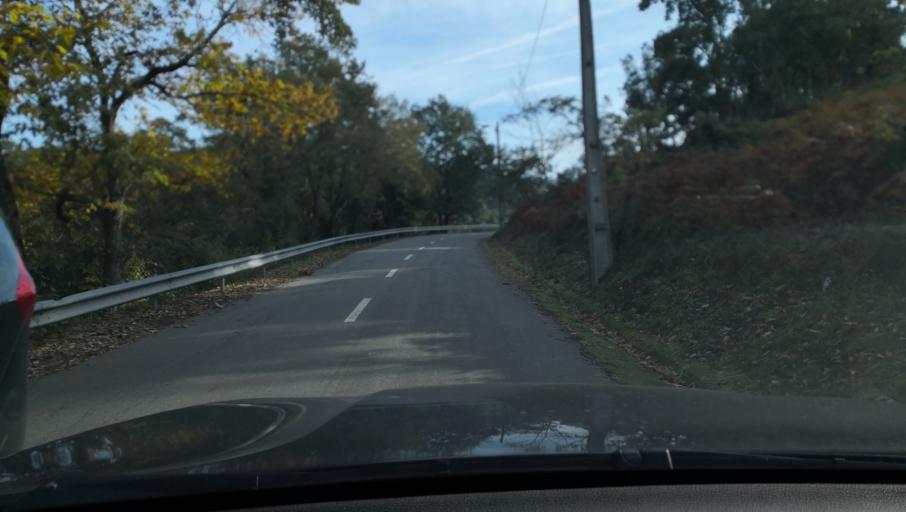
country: PT
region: Vila Real
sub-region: Vila Real
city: Vila Real
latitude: 41.2877
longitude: -7.7053
